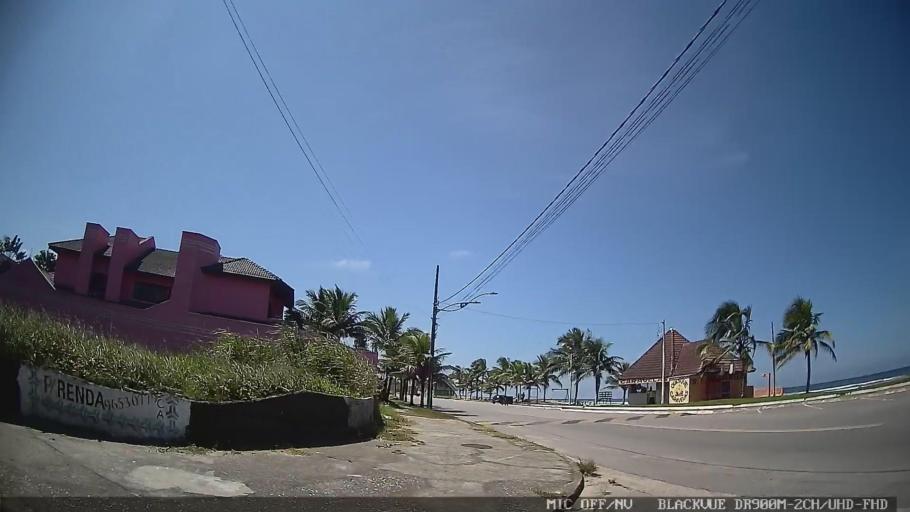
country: BR
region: Sao Paulo
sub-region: Peruibe
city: Peruibe
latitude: -24.3028
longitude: -46.9712
